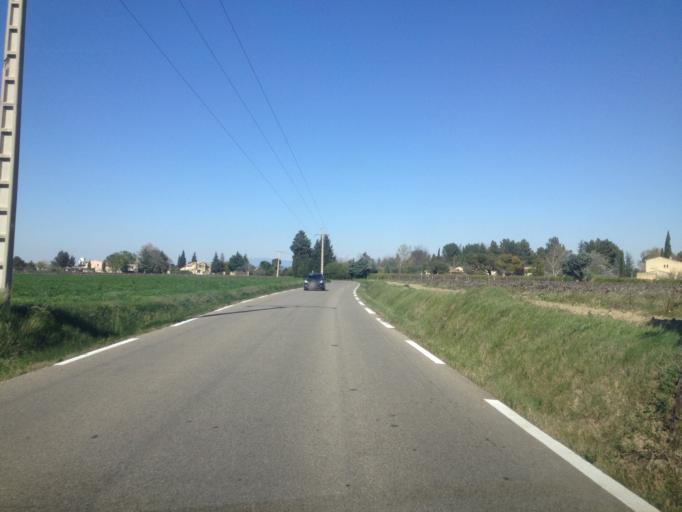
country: FR
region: Provence-Alpes-Cote d'Azur
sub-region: Departement du Vaucluse
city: Serignan-du-Comtat
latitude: 44.1627
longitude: 4.8317
